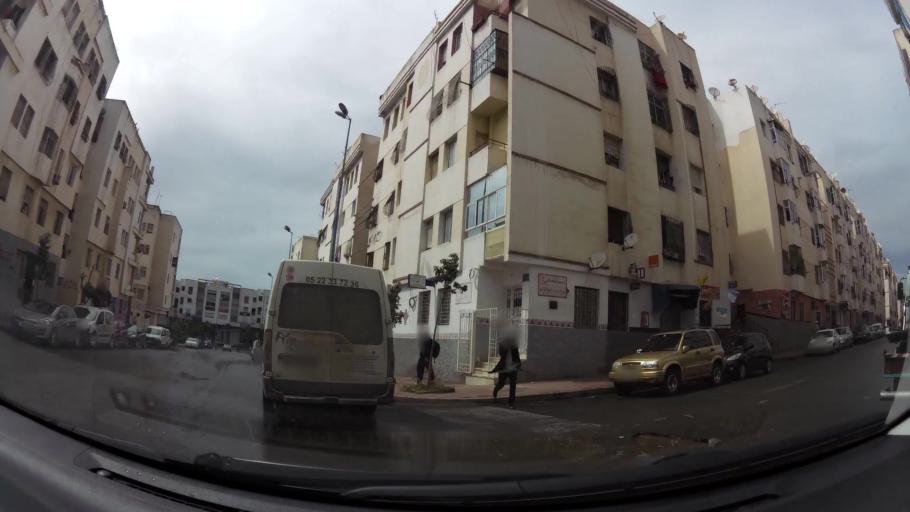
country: MA
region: Grand Casablanca
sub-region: Casablanca
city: Casablanca
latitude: 33.5285
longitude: -7.6477
